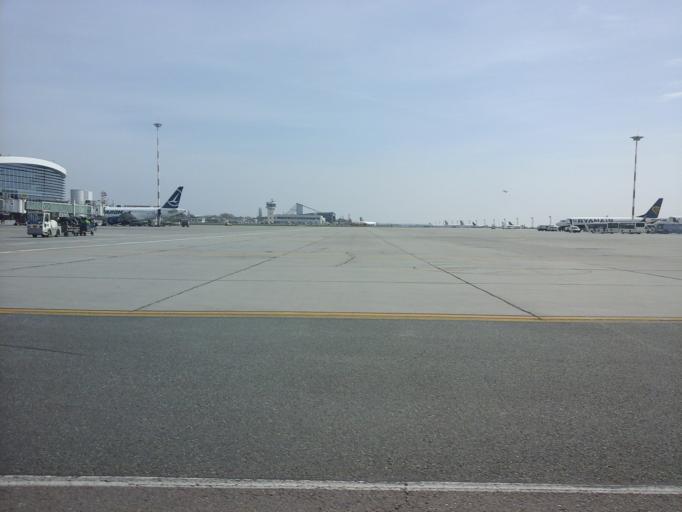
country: RO
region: Ilfov
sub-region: Comuna Otopeni
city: Otopeni
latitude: 44.5694
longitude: 26.0788
